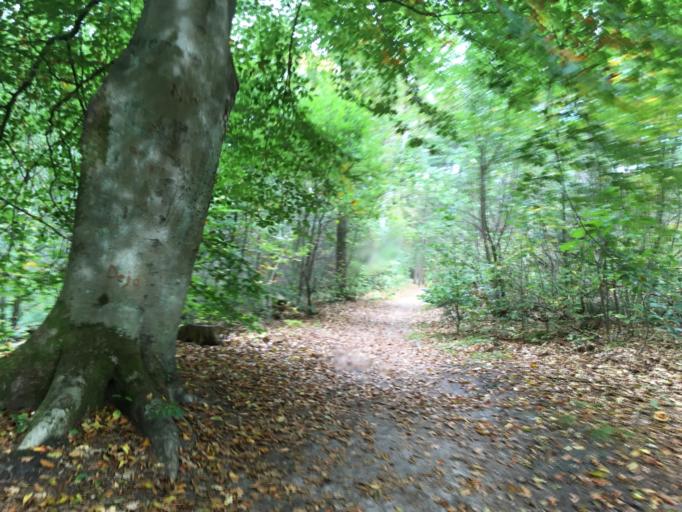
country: DE
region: Brandenburg
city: Birkenwerder
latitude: 52.7049
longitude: 13.3165
